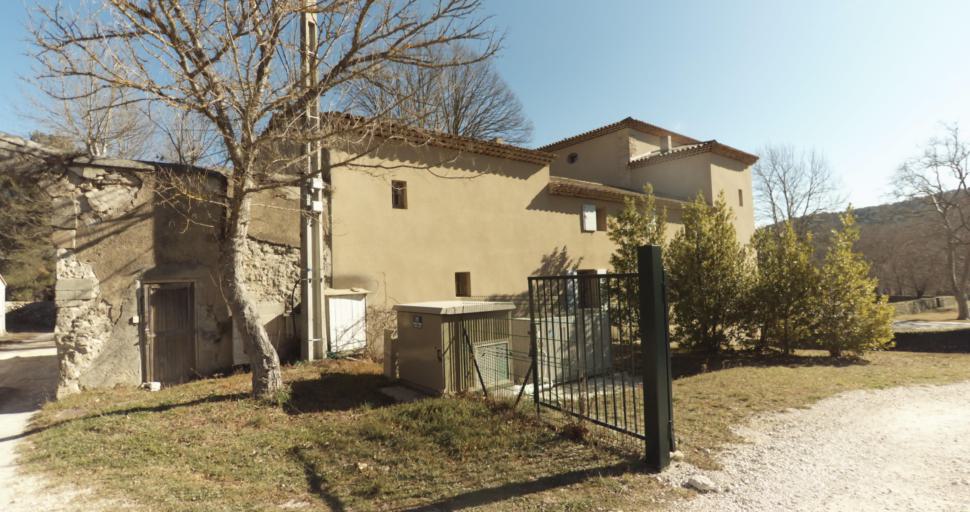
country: FR
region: Provence-Alpes-Cote d'Azur
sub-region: Departement des Bouches-du-Rhone
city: Peypin
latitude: 43.3971
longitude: 5.5657
